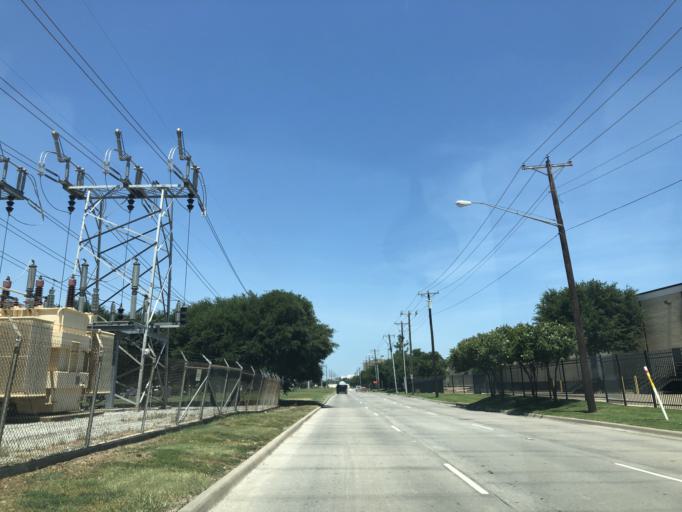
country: US
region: Texas
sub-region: Dallas County
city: Irving
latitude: 32.8295
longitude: -96.8834
